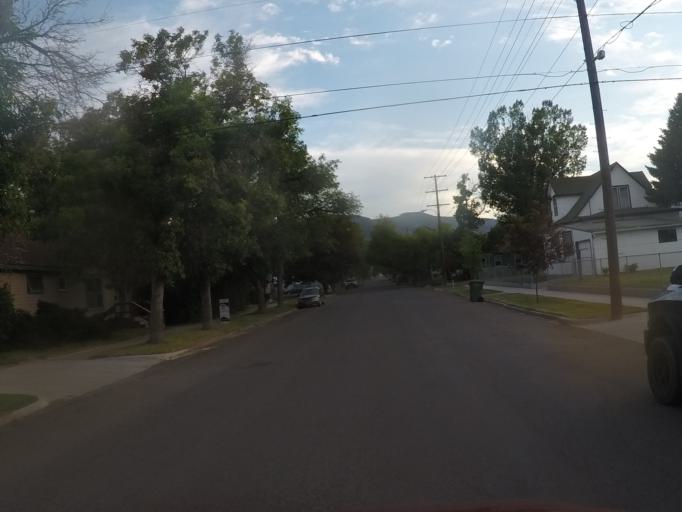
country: US
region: Montana
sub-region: Park County
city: Livingston
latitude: 45.6551
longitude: -110.5628
